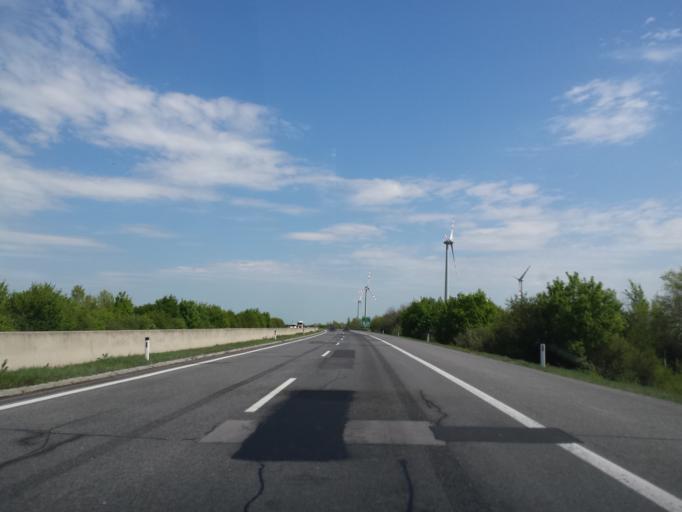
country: AT
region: Burgenland
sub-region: Politischer Bezirk Neusiedl am See
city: Nickelsdorf
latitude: 47.9188
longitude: 17.0500
